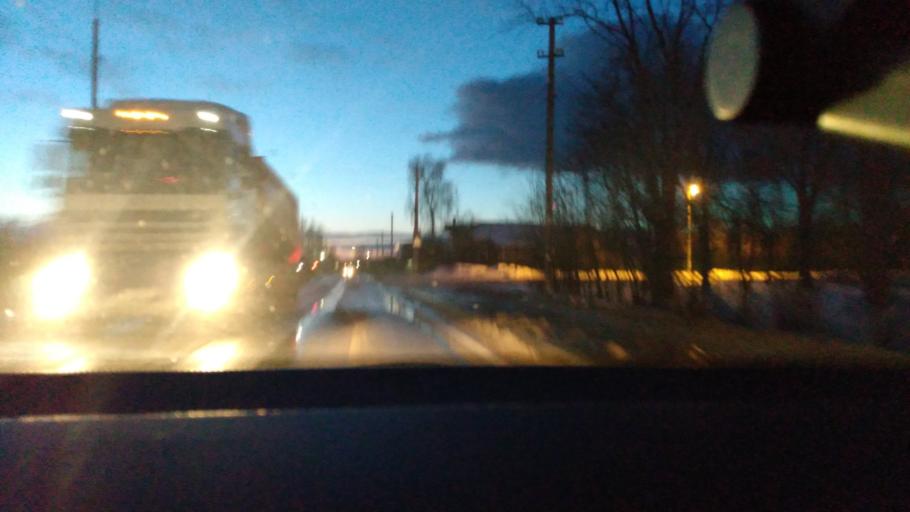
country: RU
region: Moskovskaya
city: Krasnaya Poyma
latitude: 55.1349
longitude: 39.1576
